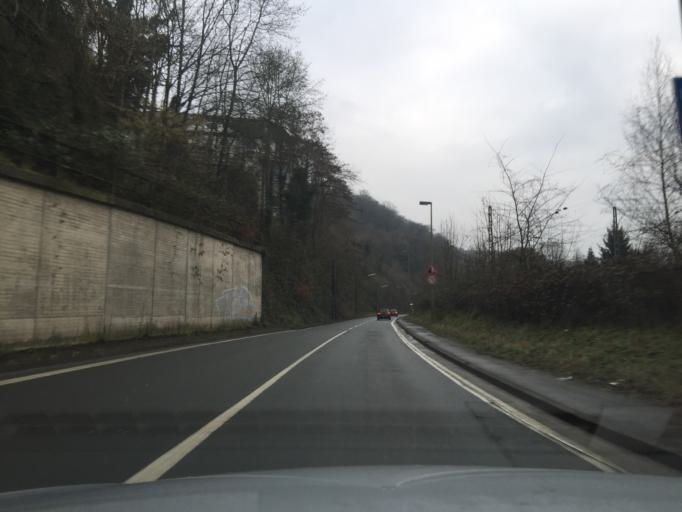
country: DE
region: North Rhine-Westphalia
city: Wetter (Ruhr)
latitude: 51.3720
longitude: 7.3881
